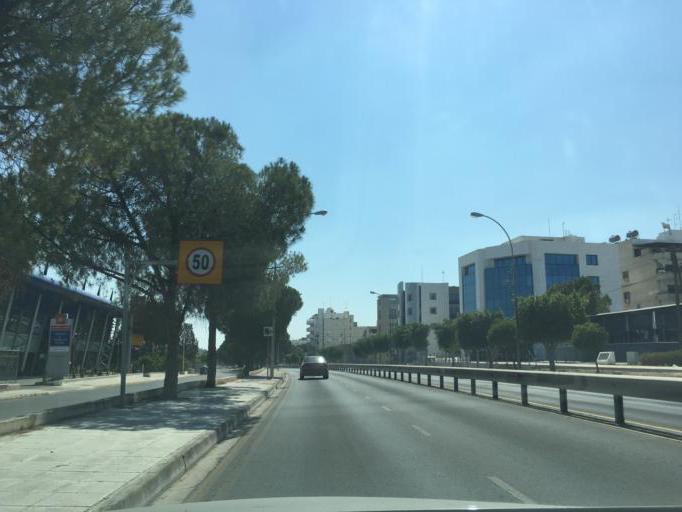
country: CY
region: Lefkosia
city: Nicosia
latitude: 35.1646
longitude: 33.3218
